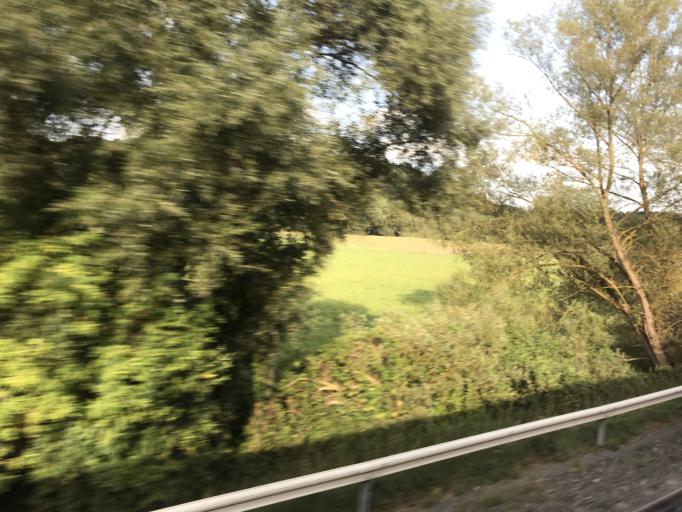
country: DE
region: Hesse
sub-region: Regierungsbezirk Giessen
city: Runkel
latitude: 50.3682
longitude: 8.1367
